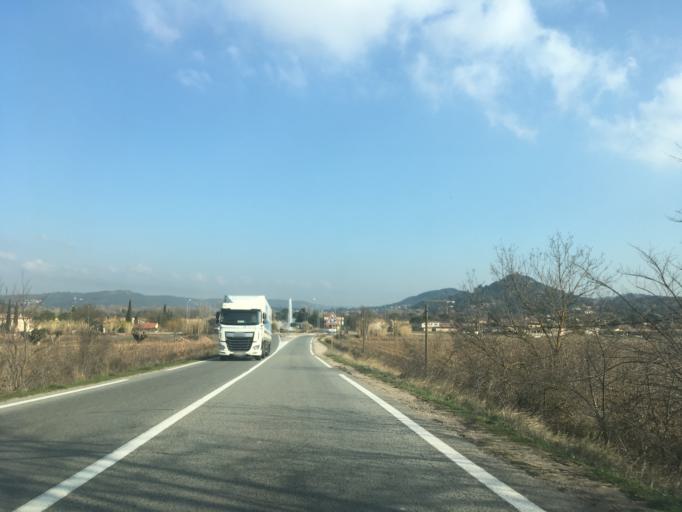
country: FR
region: Provence-Alpes-Cote d'Azur
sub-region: Departement du Var
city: Vidauban
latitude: 43.4125
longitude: 6.4171
